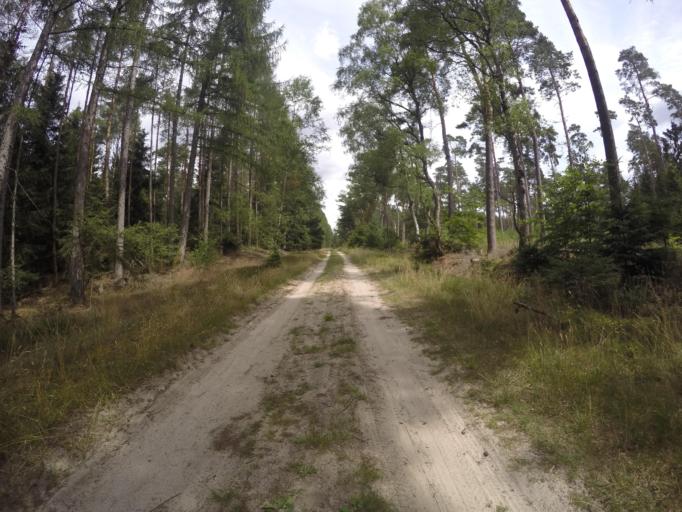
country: DE
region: Lower Saxony
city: Thomasburg
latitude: 53.2492
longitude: 10.6803
